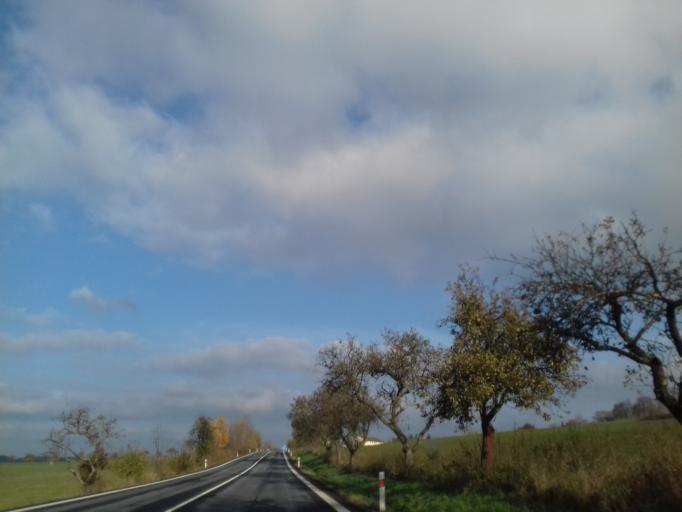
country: CZ
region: Plzensky
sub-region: Okres Domazlice
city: Klenci pod Cerchovem
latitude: 49.4529
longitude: 12.8602
